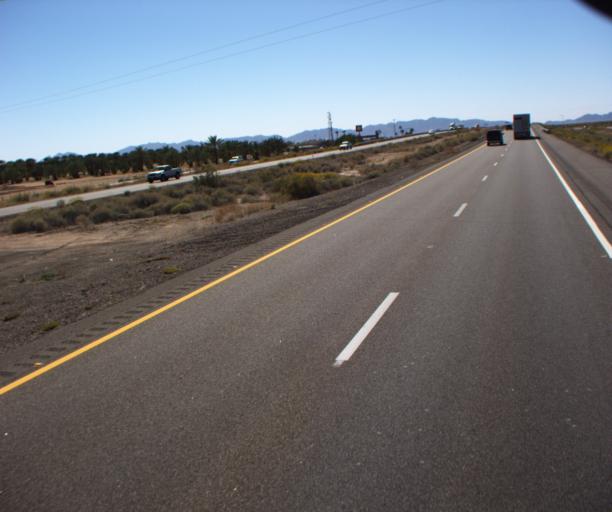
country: US
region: Arizona
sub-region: Yuma County
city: Wellton
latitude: 32.8023
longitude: -113.5368
